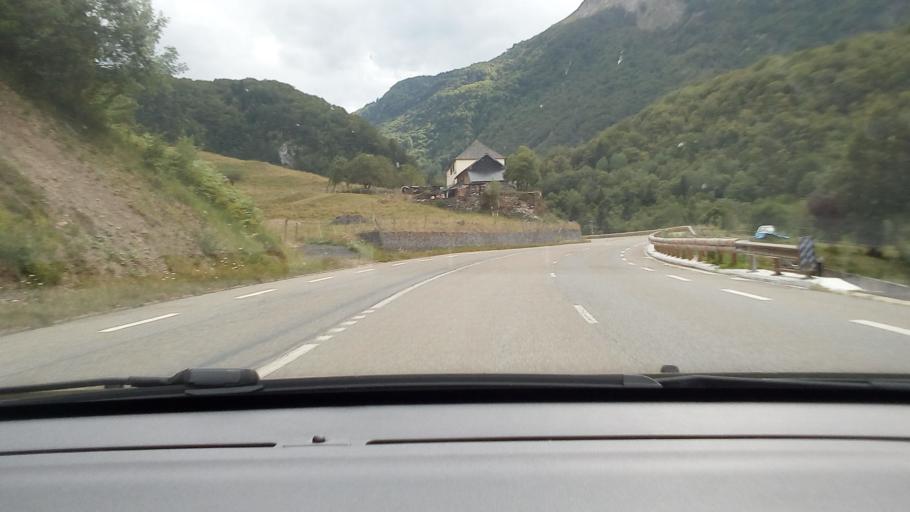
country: ES
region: Aragon
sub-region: Provincia de Huesca
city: Canfranc
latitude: 42.8448
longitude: -0.5516
